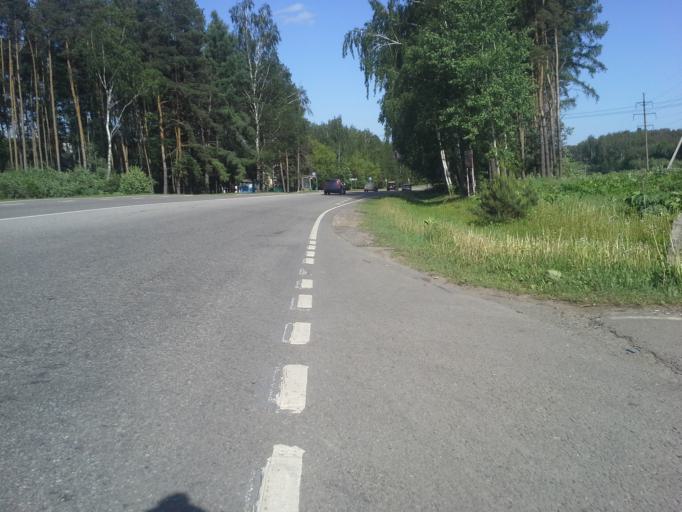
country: RU
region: Moskovskaya
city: Troitsk
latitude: 55.4327
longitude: 37.3342
